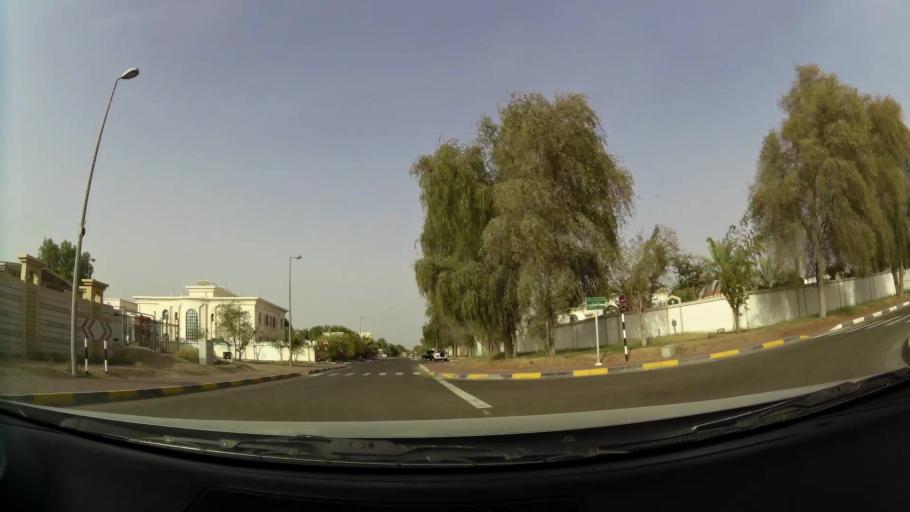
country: AE
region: Abu Dhabi
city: Al Ain
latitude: 24.2274
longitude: 55.6665
